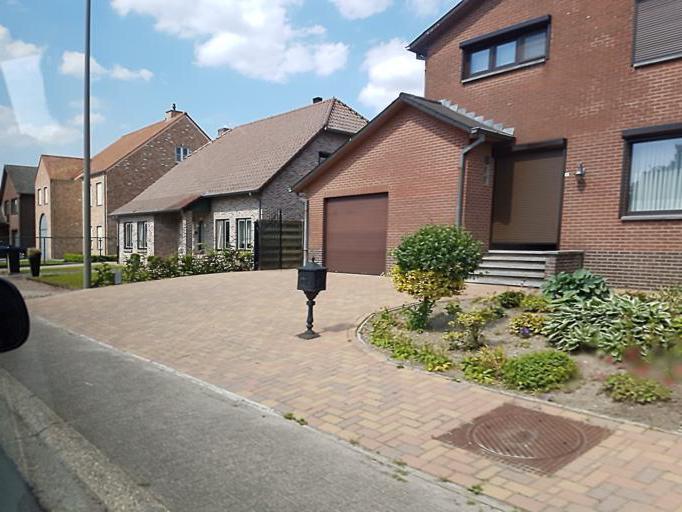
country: BE
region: Flanders
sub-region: Provincie Limburg
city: Neerpelt
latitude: 51.1979
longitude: 5.5053
